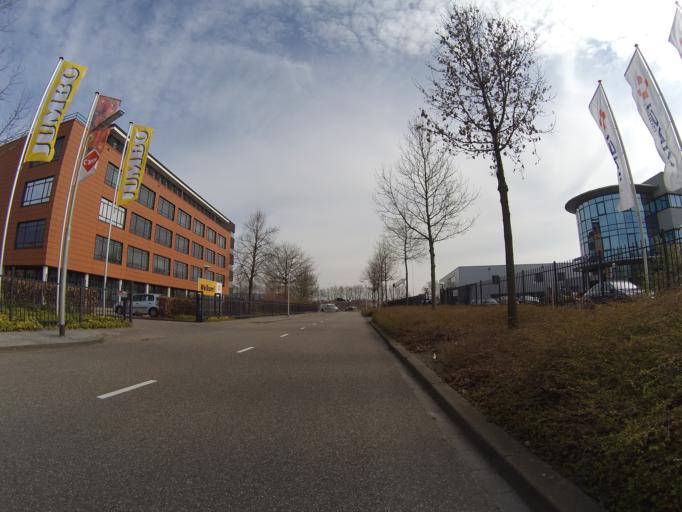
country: NL
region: Utrecht
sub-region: Gemeente Amersfoort
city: Randenbroek
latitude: 52.1797
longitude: 5.4196
